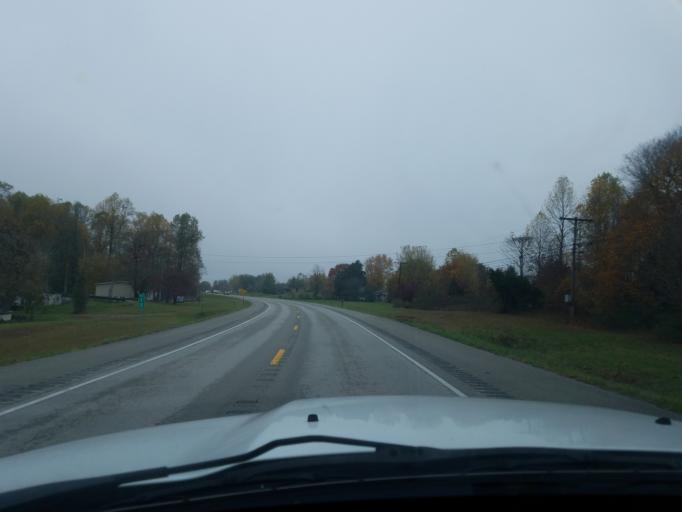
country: US
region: Kentucky
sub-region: Taylor County
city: Campbellsville
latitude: 37.3838
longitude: -85.4154
